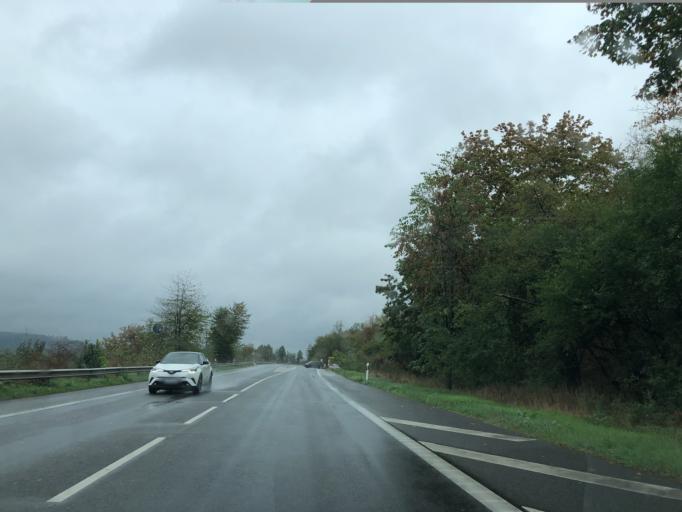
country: DE
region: North Rhine-Westphalia
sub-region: Regierungsbezirk Dusseldorf
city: Grevenbroich
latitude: 51.0817
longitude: 6.5552
